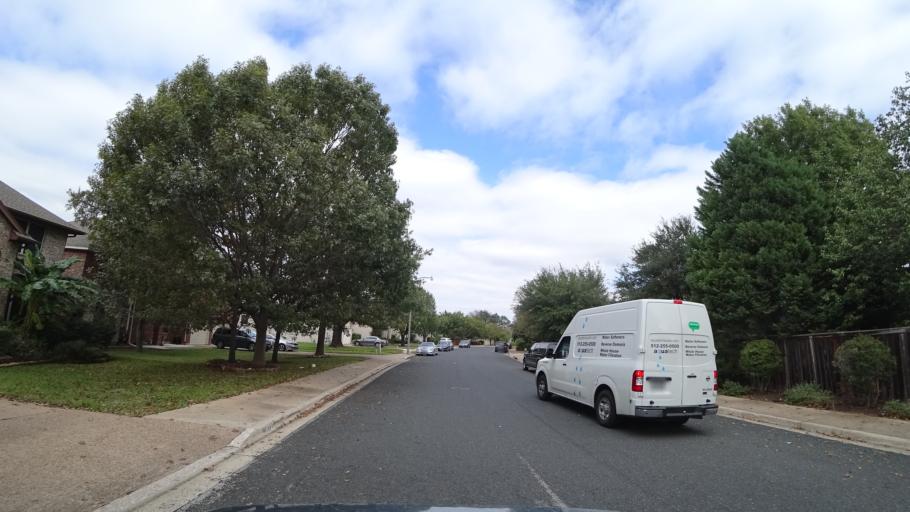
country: US
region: Texas
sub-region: Williamson County
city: Brushy Creek
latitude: 30.5155
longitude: -97.7414
